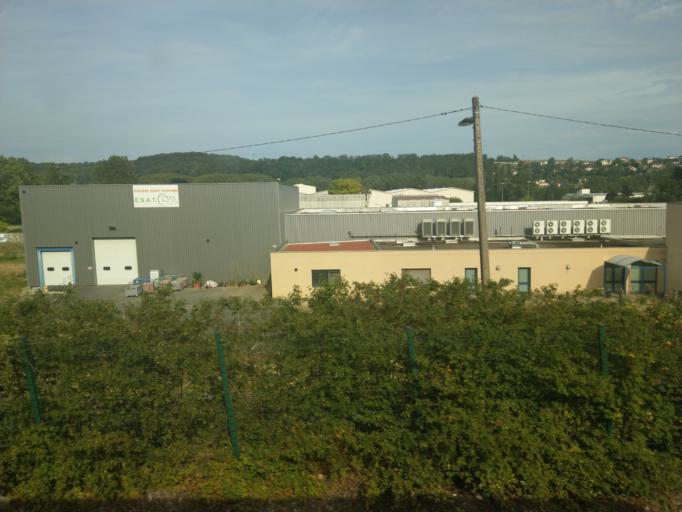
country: FR
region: Rhone-Alpes
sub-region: Departement du Rhone
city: Albigny-sur-Saone
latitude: 45.8537
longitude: 4.8311
